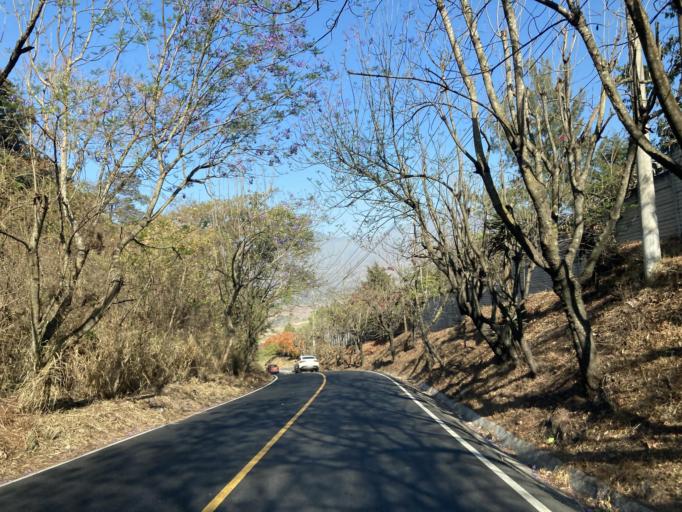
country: GT
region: Guatemala
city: Amatitlan
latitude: 14.5000
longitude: -90.6189
